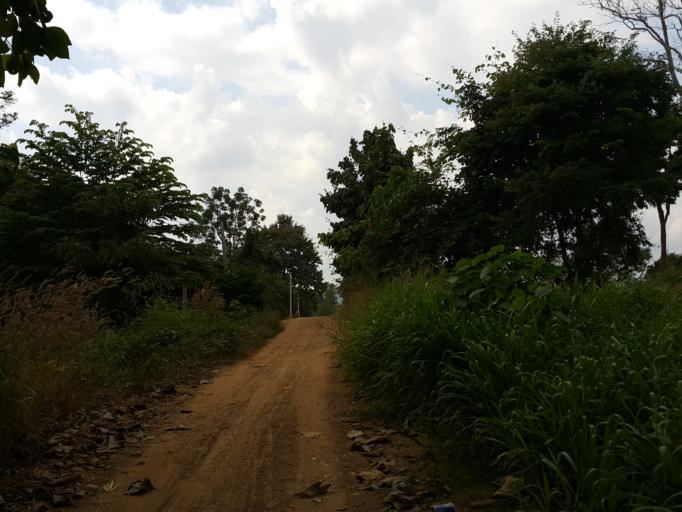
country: TH
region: Sukhothai
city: Thung Saliam
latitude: 17.4083
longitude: 99.5845
